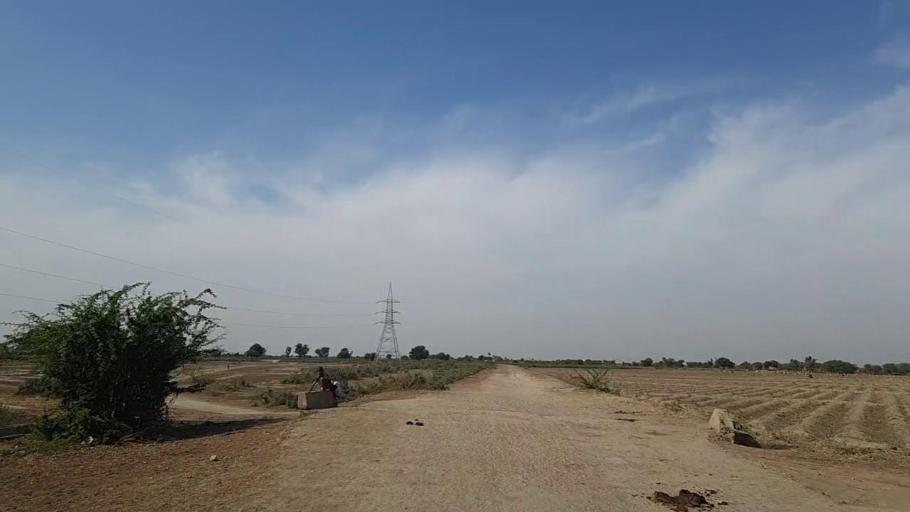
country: PK
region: Sindh
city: Samaro
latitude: 25.2216
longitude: 69.4500
